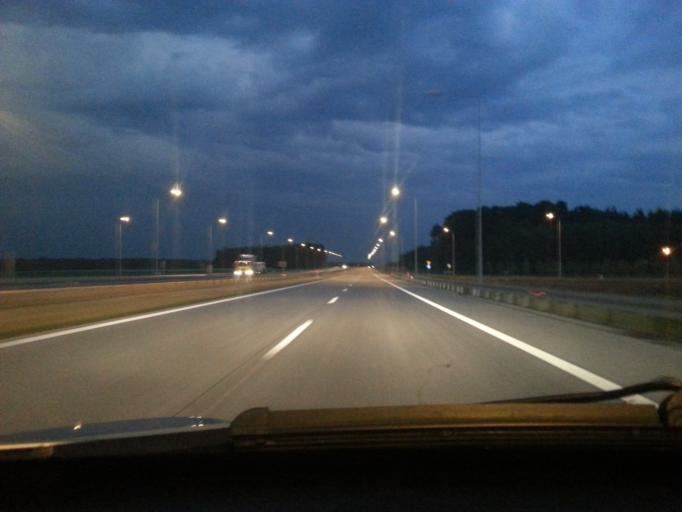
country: PL
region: Lodz Voivodeship
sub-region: Powiat sieradzki
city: Sieradz
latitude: 51.5268
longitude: 18.6952
